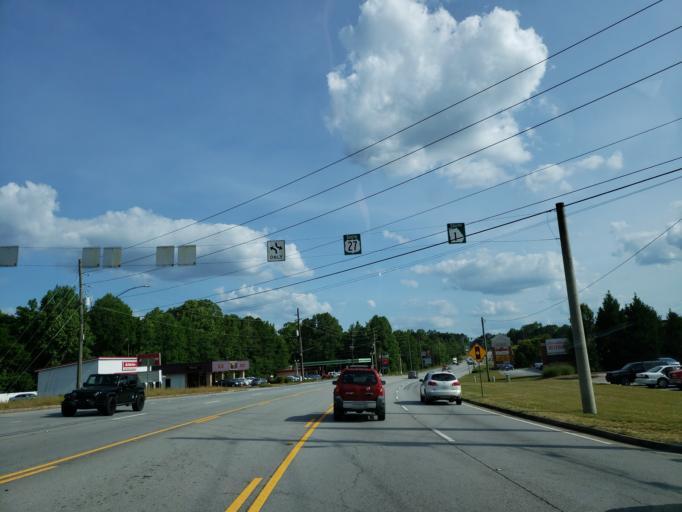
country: US
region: Georgia
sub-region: Carroll County
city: Carrollton
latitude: 33.6013
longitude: -85.0791
